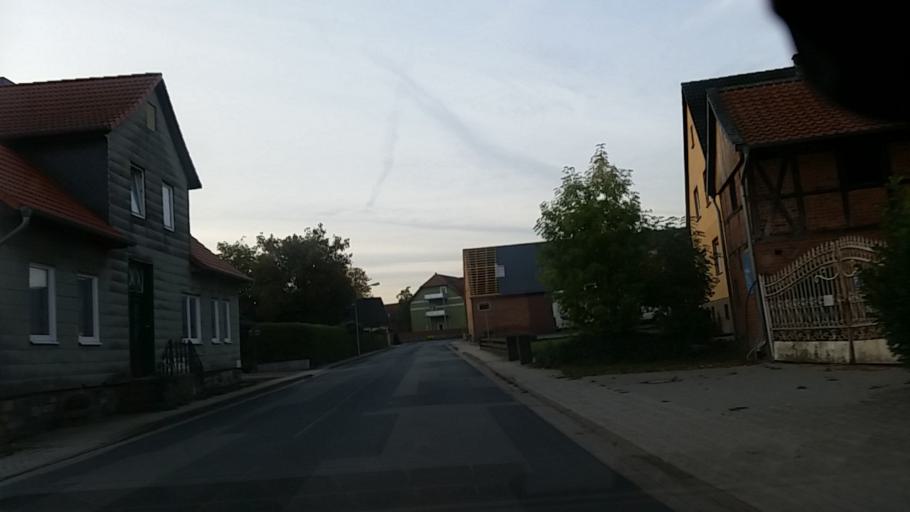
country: DE
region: Lower Saxony
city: Tiddische
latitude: 52.5012
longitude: 10.8018
